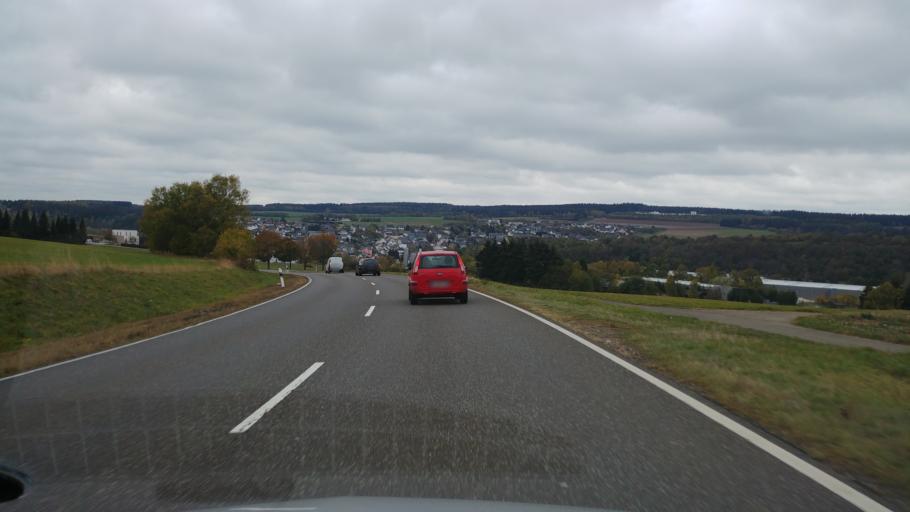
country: DE
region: Rheinland-Pfalz
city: Thalfang
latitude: 49.7471
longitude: 7.0150
